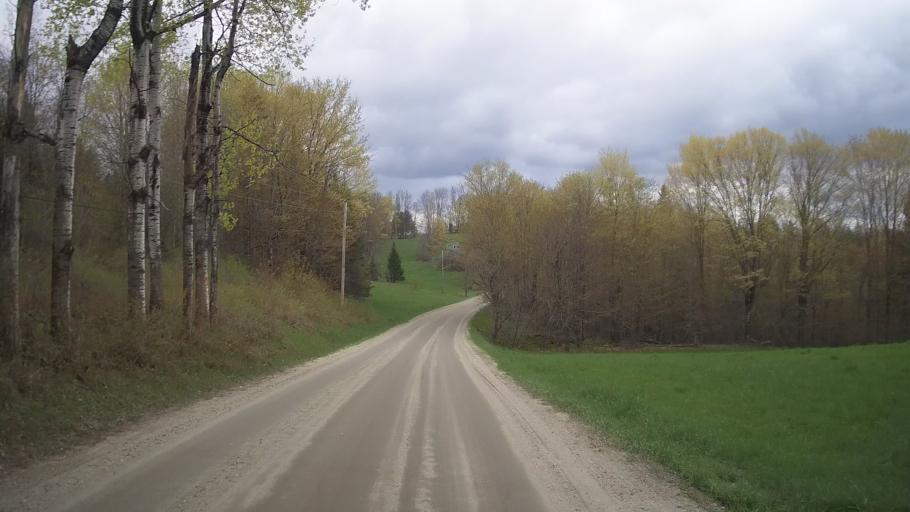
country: US
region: Vermont
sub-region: Caledonia County
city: Lyndonville
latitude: 44.6043
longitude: -71.9503
